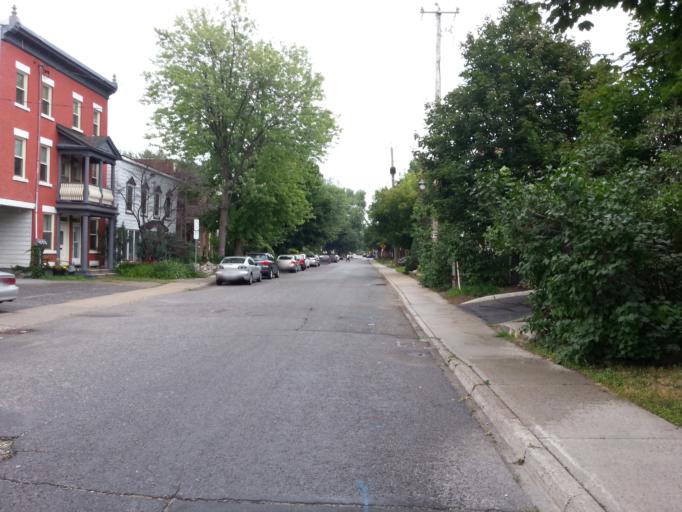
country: CA
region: Ontario
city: Ottawa
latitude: 45.4335
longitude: -75.6949
